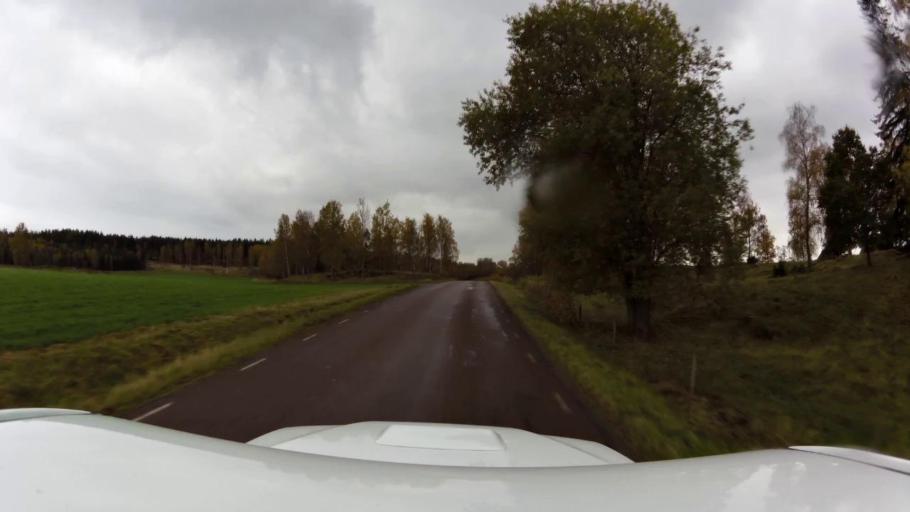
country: SE
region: OEstergoetland
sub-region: Linkopings Kommun
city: Ljungsbro
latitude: 58.5335
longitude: 15.5246
